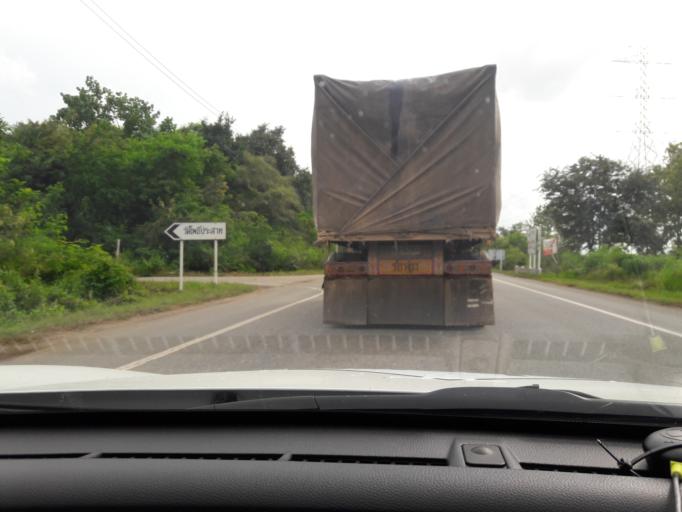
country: TH
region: Nakhon Sawan
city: Tak Fa
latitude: 15.4131
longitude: 100.5147
